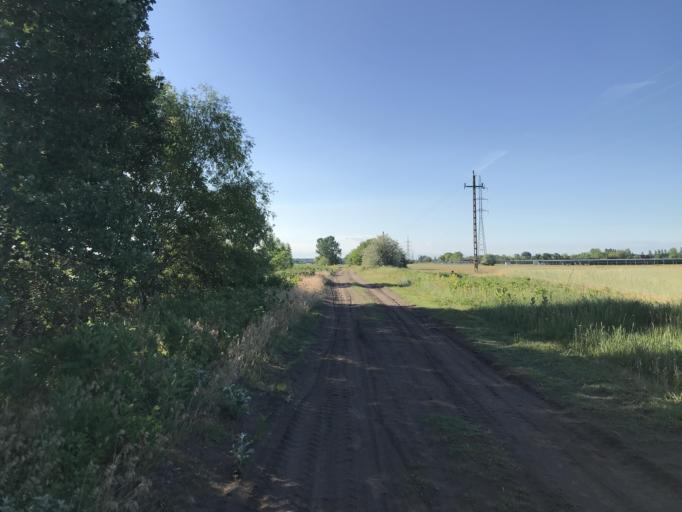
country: HU
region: Bacs-Kiskun
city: Tiszakecske
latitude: 46.9614
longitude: 20.0779
